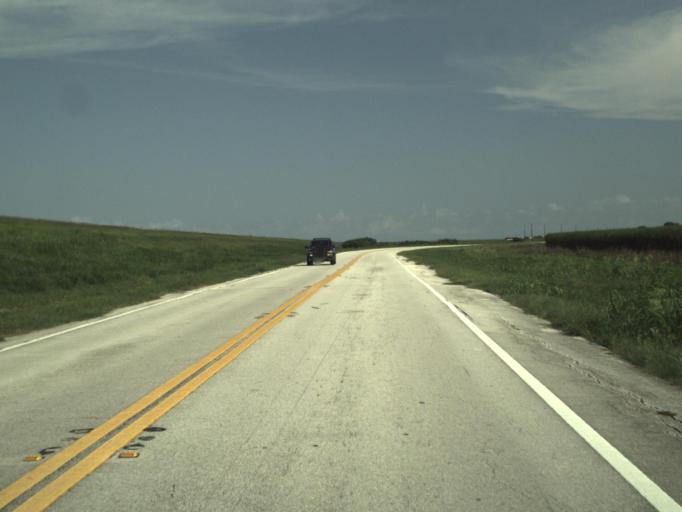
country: US
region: Florida
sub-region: Palm Beach County
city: Pahokee
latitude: 26.7651
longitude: -80.6882
